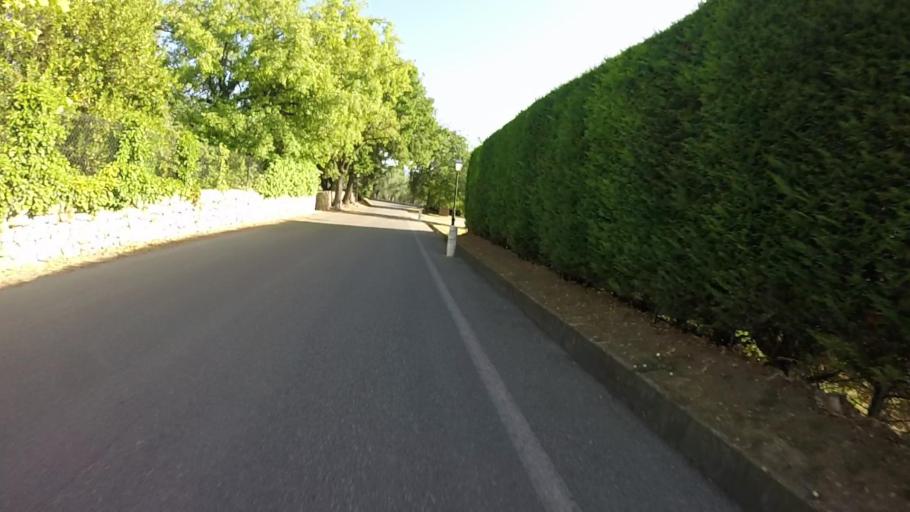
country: FR
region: Provence-Alpes-Cote d'Azur
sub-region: Departement des Alpes-Maritimes
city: Chateauneuf-Grasse
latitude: 43.6532
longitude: 6.9857
